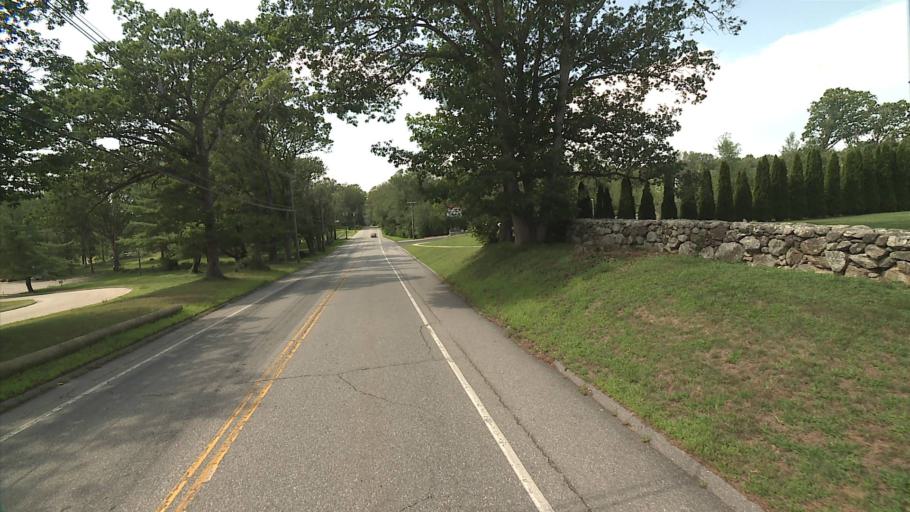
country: US
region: Connecticut
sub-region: New London County
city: Colchester
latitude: 41.5811
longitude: -72.3511
